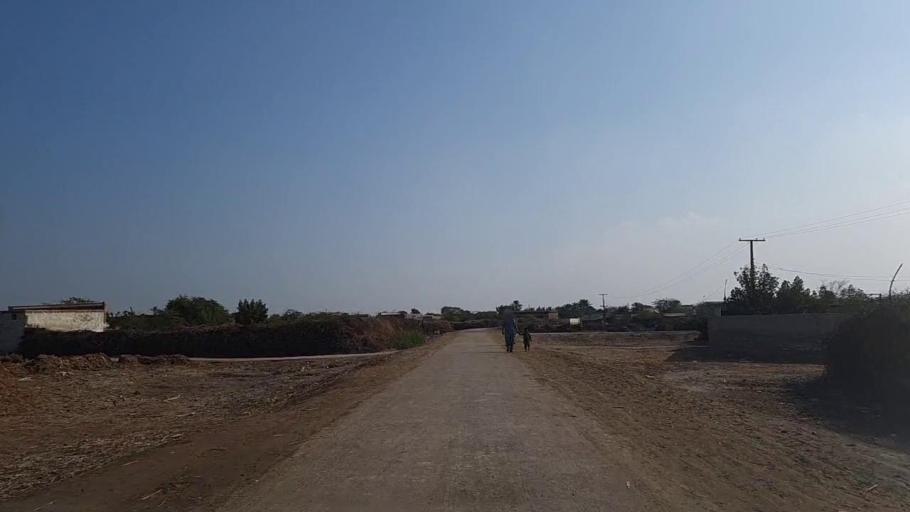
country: PK
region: Sindh
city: Jam Sahib
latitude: 26.2761
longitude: 68.5833
